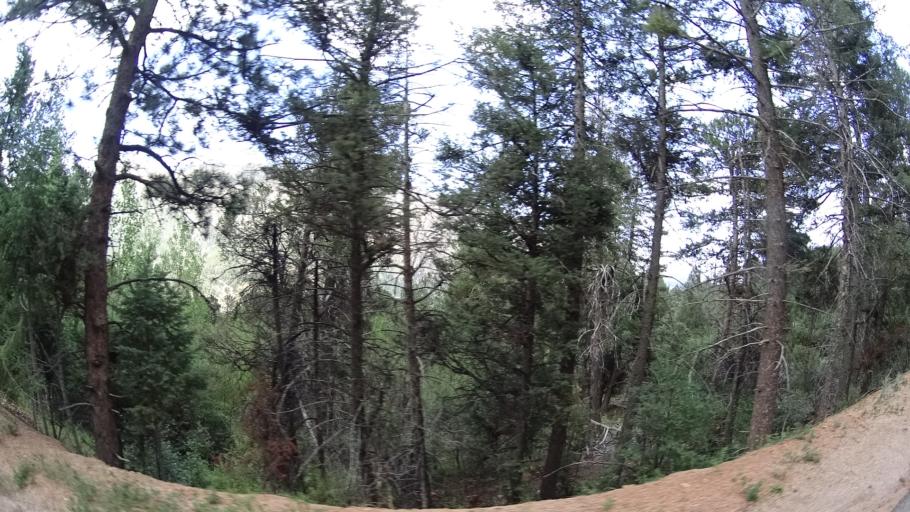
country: US
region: Colorado
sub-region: El Paso County
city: Cascade-Chipita Park
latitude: 38.9076
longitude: -104.9837
